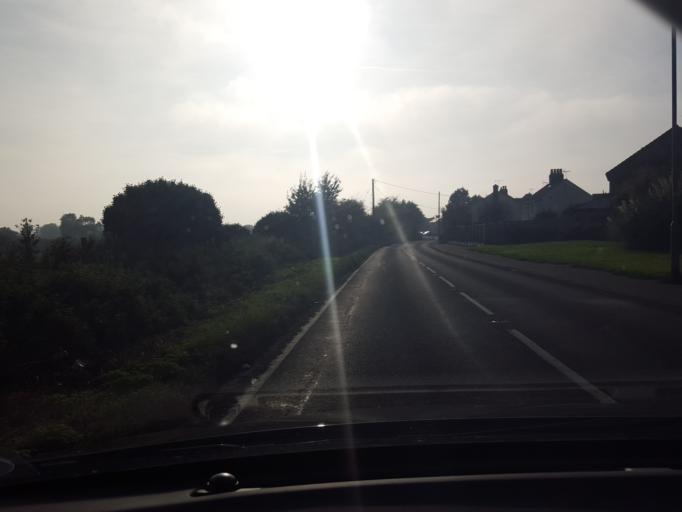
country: GB
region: England
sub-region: Essex
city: Dovercourt
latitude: 51.9258
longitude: 1.2340
